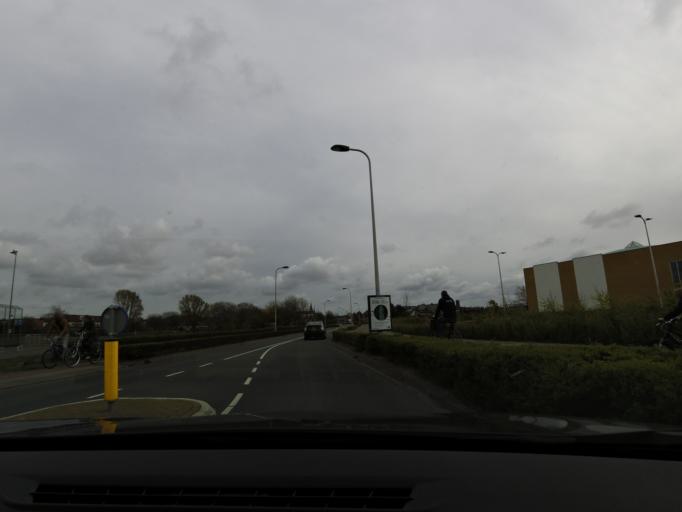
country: NL
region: South Holland
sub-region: Gemeente Noordwijk
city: Noordwijk-Binnen
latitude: 52.2407
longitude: 4.4411
